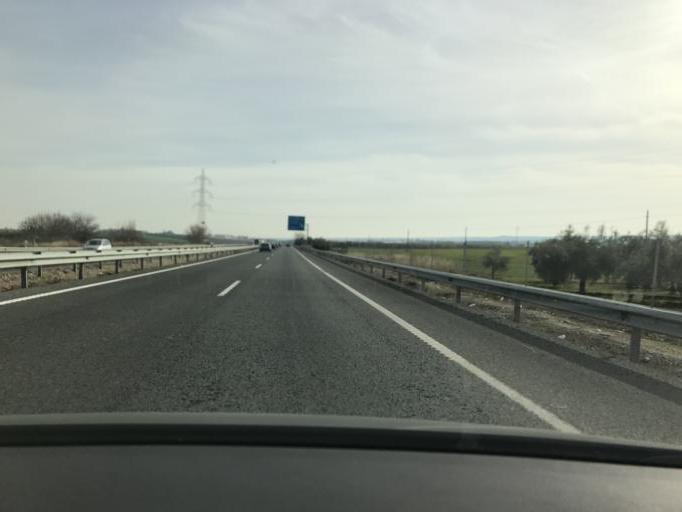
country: ES
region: Andalusia
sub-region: Provincia de Granada
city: Moraleda de Zafayona
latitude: 37.1920
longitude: -3.9775
